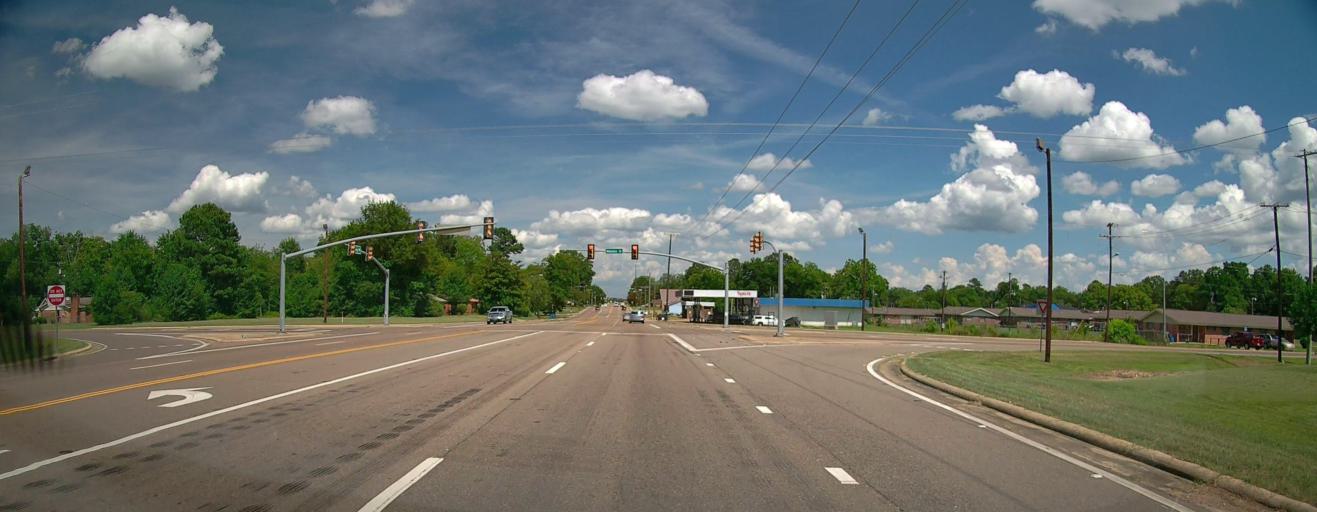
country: US
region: Mississippi
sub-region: Monroe County
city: Aberdeen
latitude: 33.8149
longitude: -88.5535
